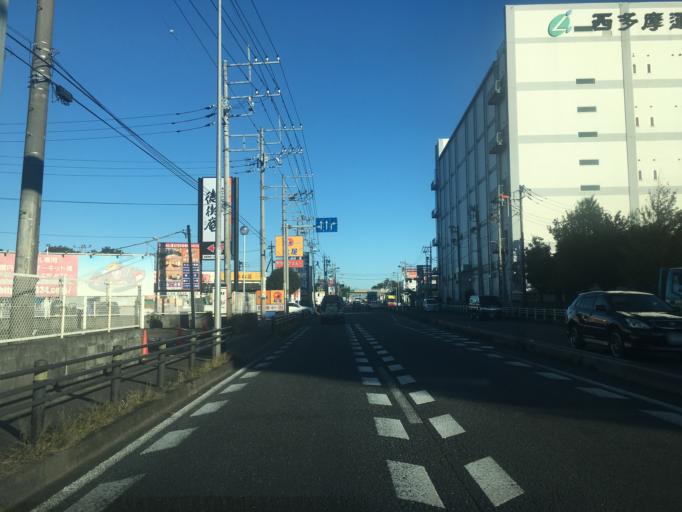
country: JP
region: Saitama
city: Sayama
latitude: 35.8110
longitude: 139.3779
